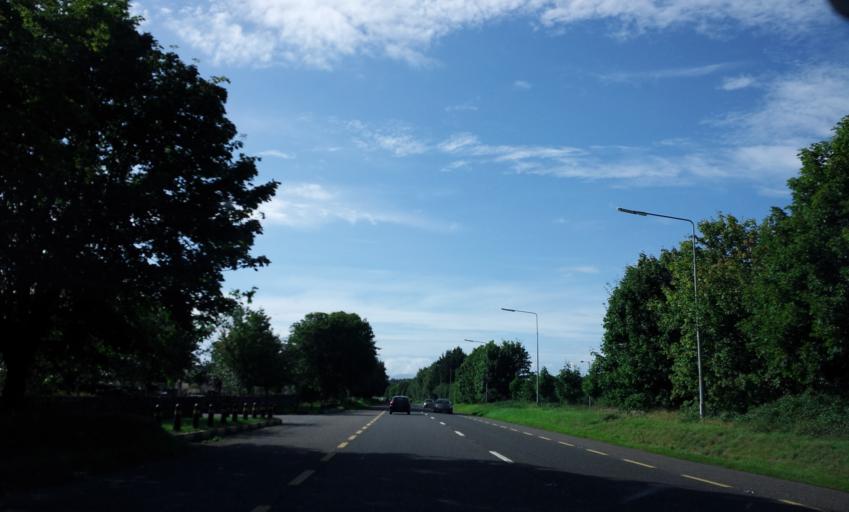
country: IE
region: Munster
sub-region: Ciarrai
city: Cill Airne
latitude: 52.0663
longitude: -9.4940
